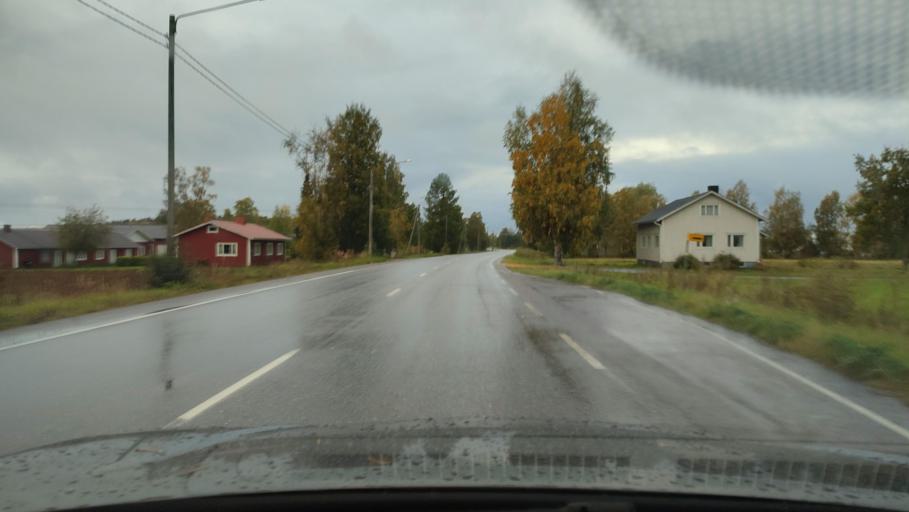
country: FI
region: Southern Ostrobothnia
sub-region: Suupohja
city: Karijoki
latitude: 62.2312
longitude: 21.6249
